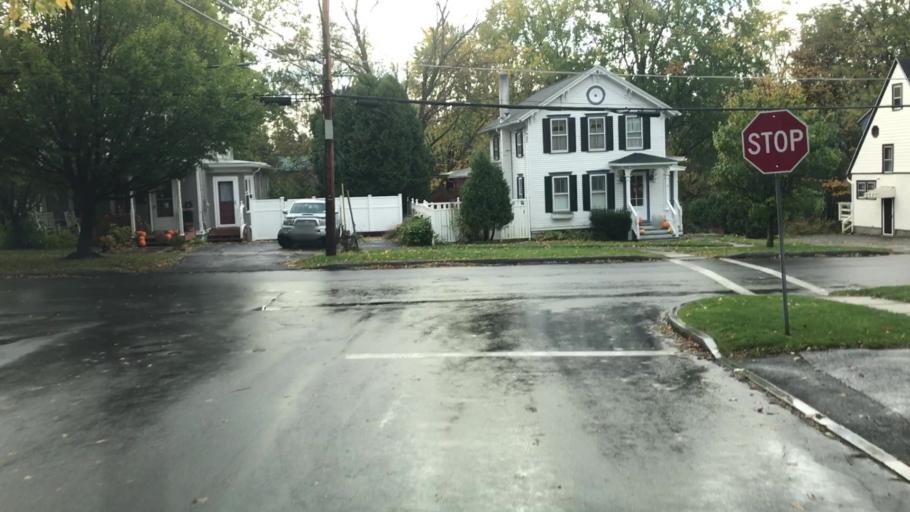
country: US
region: New York
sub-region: Onondaga County
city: Skaneateles
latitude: 42.9475
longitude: -76.4185
